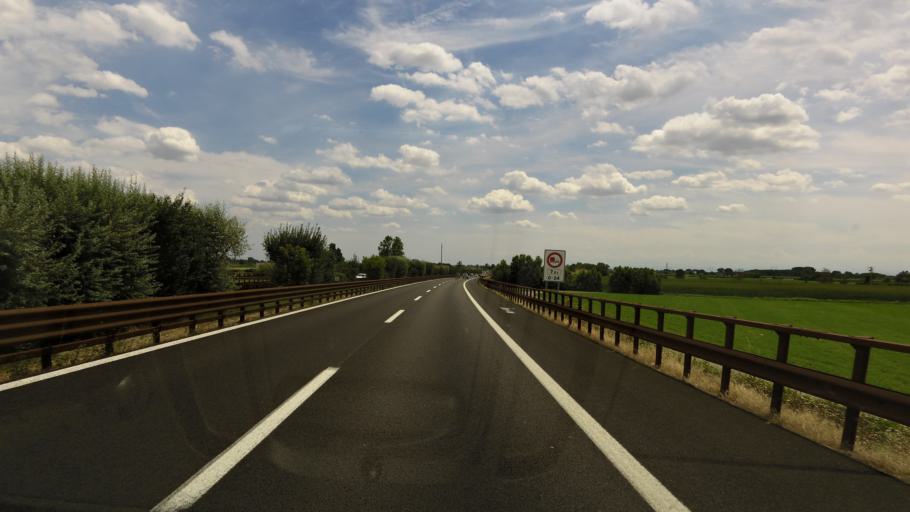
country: IT
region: Lombardy
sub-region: Provincia di Mantova
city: Pegognaga
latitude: 45.0440
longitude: 10.8529
